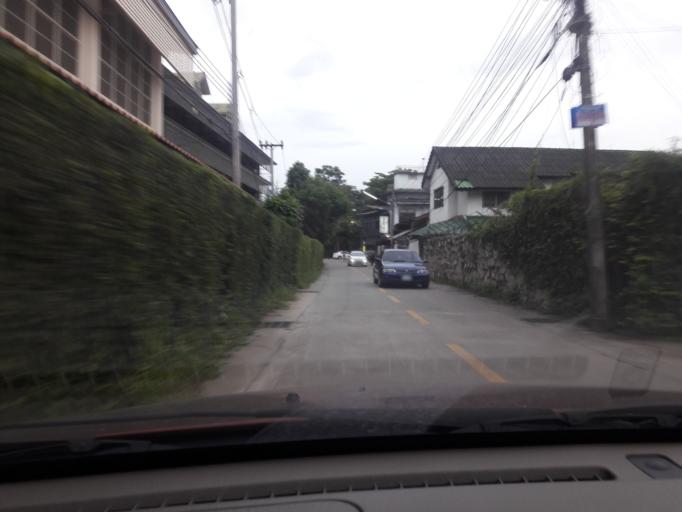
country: TH
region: Chiang Mai
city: Chiang Mai
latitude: 18.7958
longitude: 99.0030
